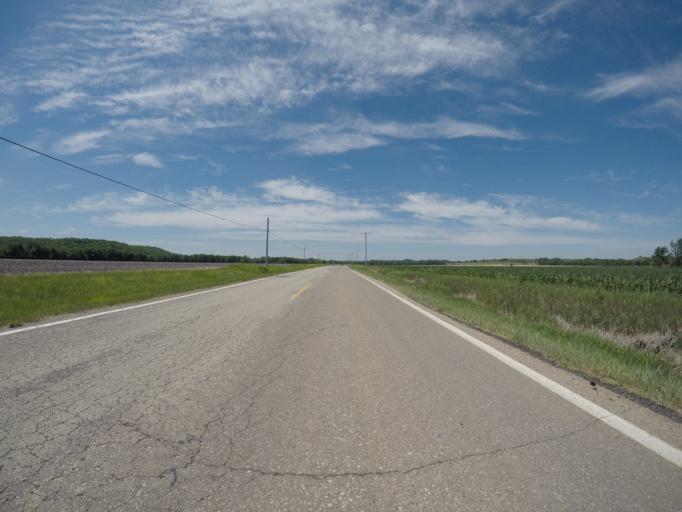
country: US
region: Kansas
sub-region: Wabaunsee County
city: Alma
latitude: 39.0450
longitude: -96.2544
